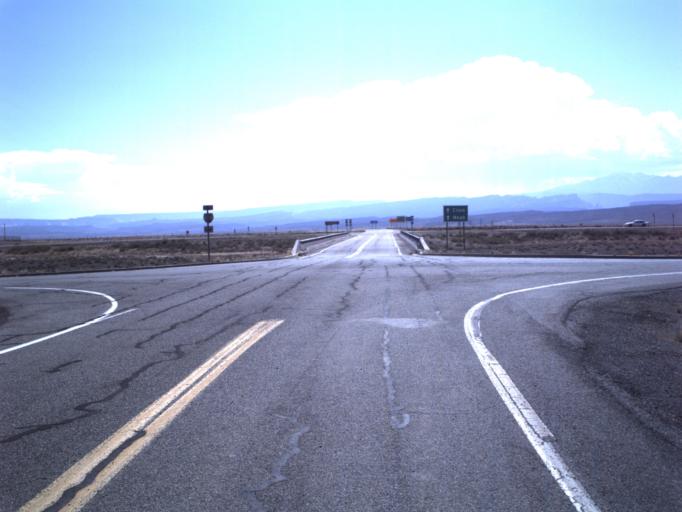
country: US
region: Utah
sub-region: Grand County
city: Moab
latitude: 38.9393
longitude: -109.4085
